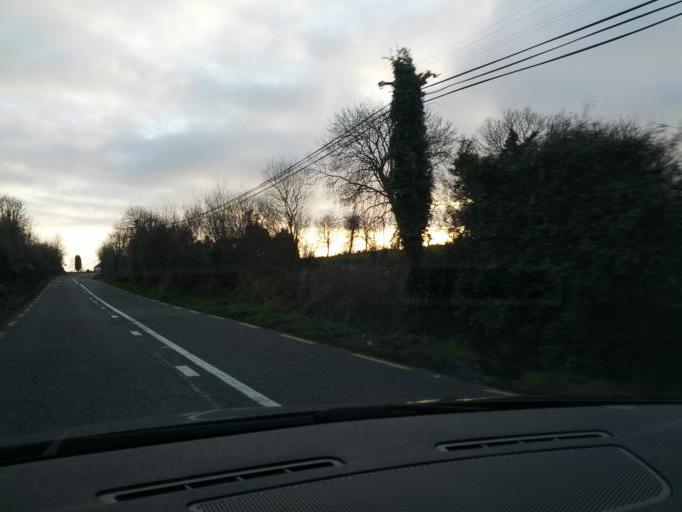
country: IE
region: Connaught
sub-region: Sligo
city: Ballymote
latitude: 54.1224
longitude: -8.5950
